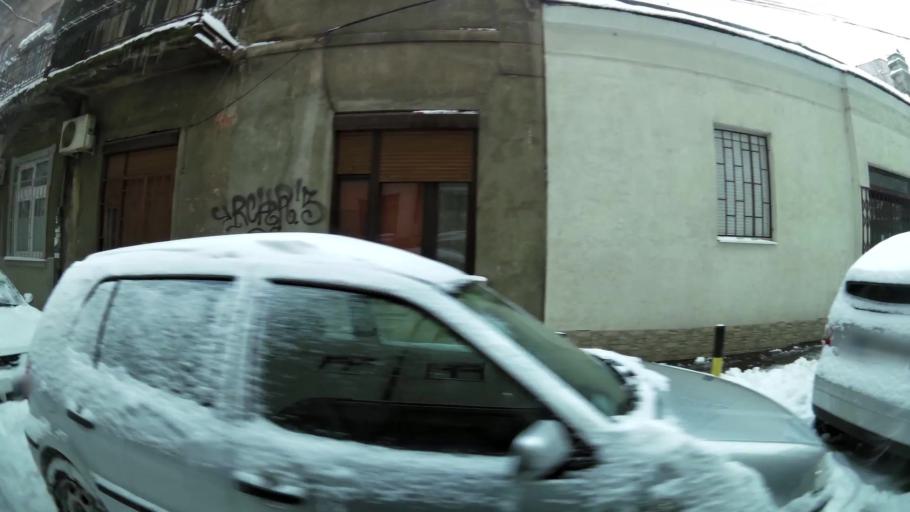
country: RS
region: Central Serbia
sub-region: Belgrade
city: Stari Grad
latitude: 44.8200
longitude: 20.4715
